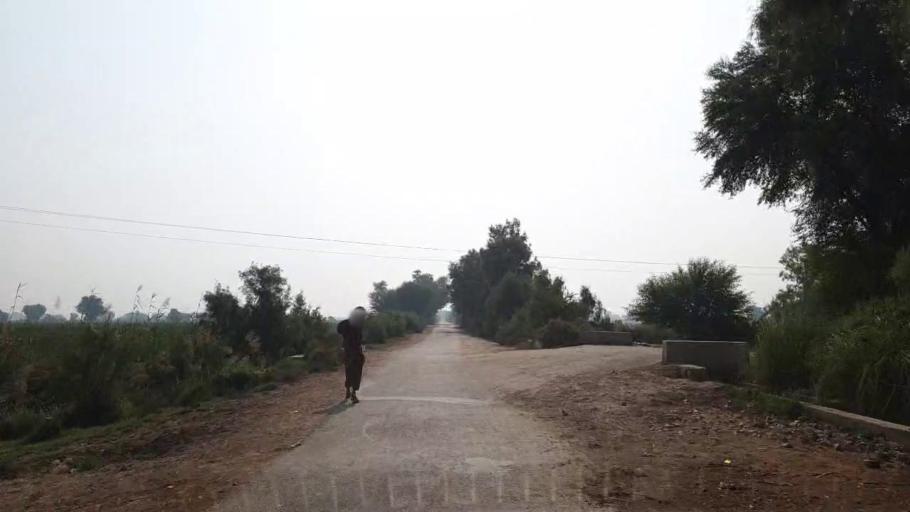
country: PK
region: Sindh
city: Sehwan
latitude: 26.4733
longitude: 67.7742
